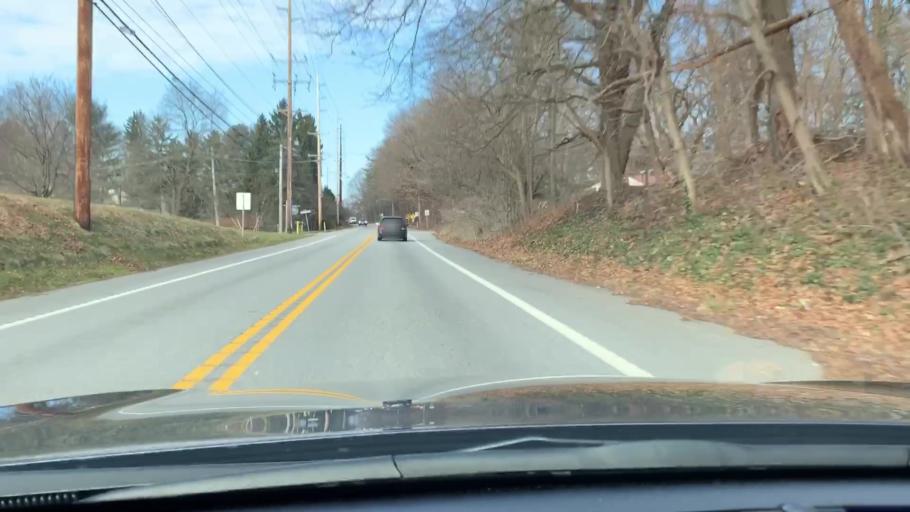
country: US
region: Pennsylvania
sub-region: Chester County
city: Paoli
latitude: 40.0330
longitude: -75.4685
